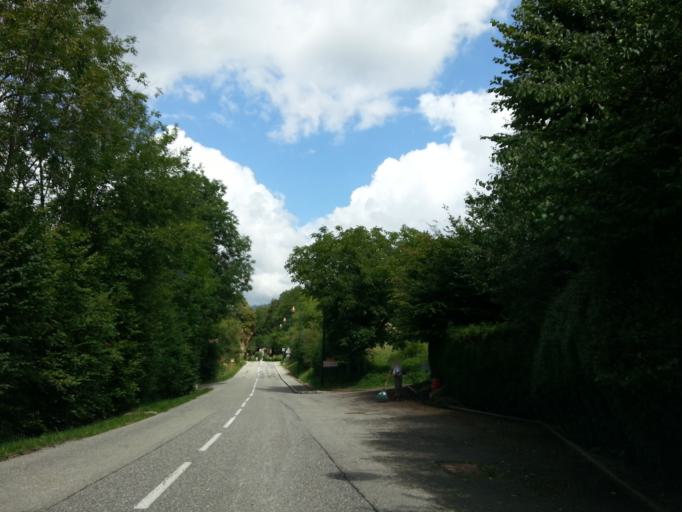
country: FR
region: Rhone-Alpes
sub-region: Departement de la Haute-Savoie
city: Menthon-Saint-Bernard
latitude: 45.8663
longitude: 6.2184
